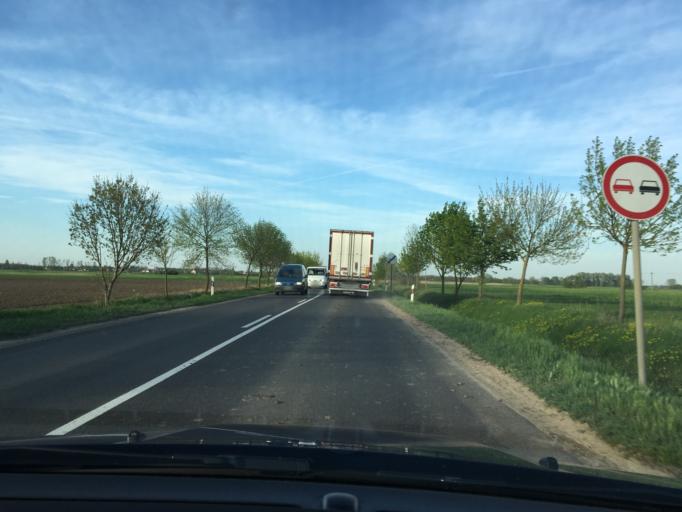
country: HU
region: Hajdu-Bihar
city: Berettyoujfalu
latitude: 47.1822
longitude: 21.5298
